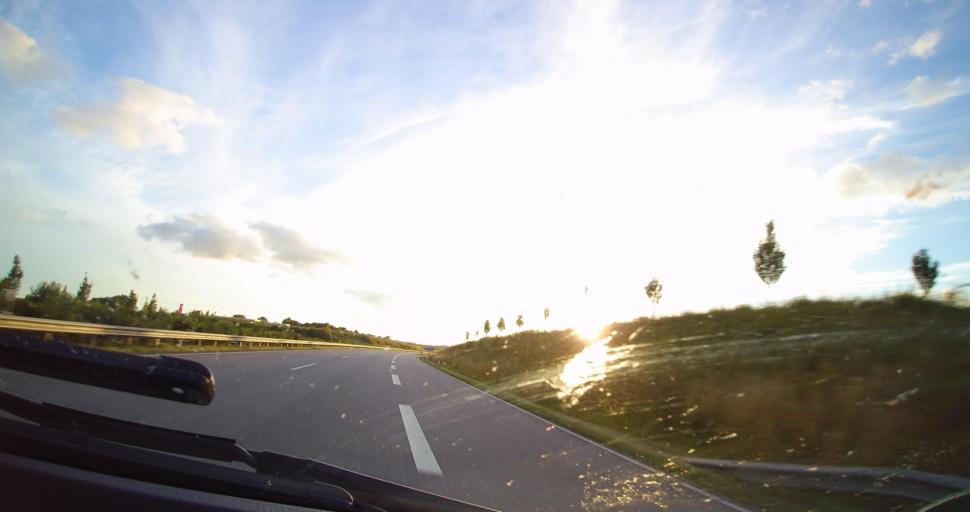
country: DE
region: Schleswig-Holstein
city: Geschendorf
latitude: 53.9226
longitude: 10.4582
